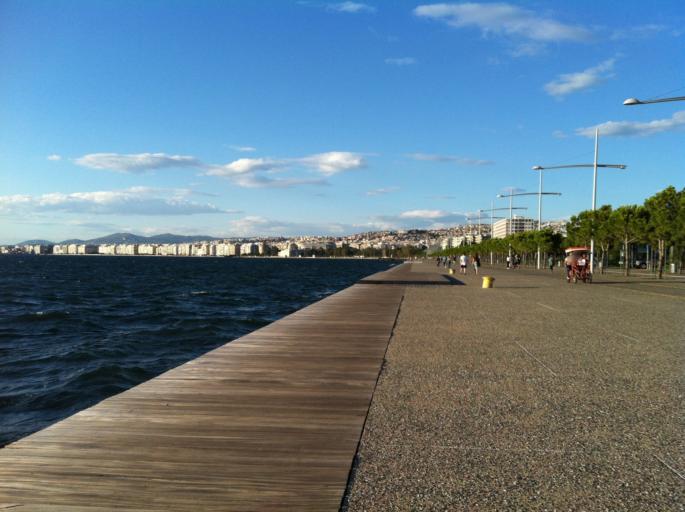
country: GR
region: Central Macedonia
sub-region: Nomos Thessalonikis
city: Triandria
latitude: 40.6129
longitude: 22.9508
